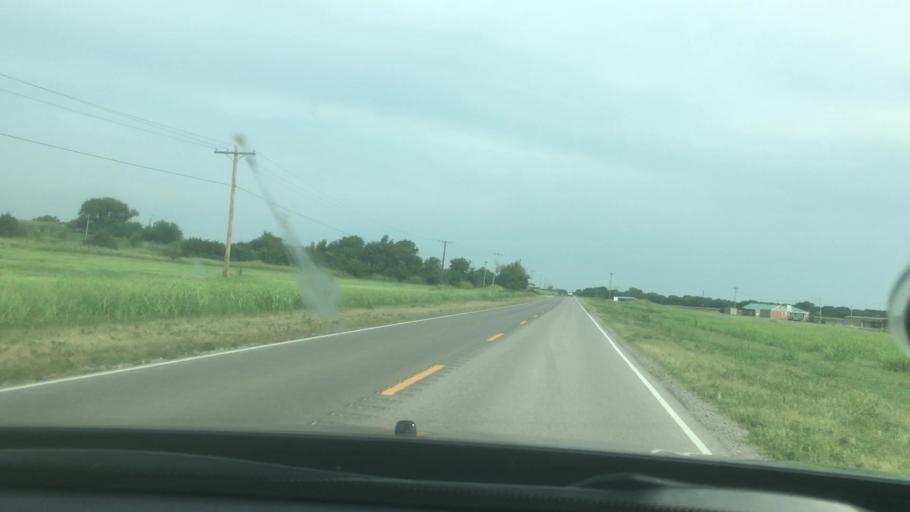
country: US
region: Oklahoma
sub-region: Garvin County
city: Maysville
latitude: 34.7985
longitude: -97.3590
